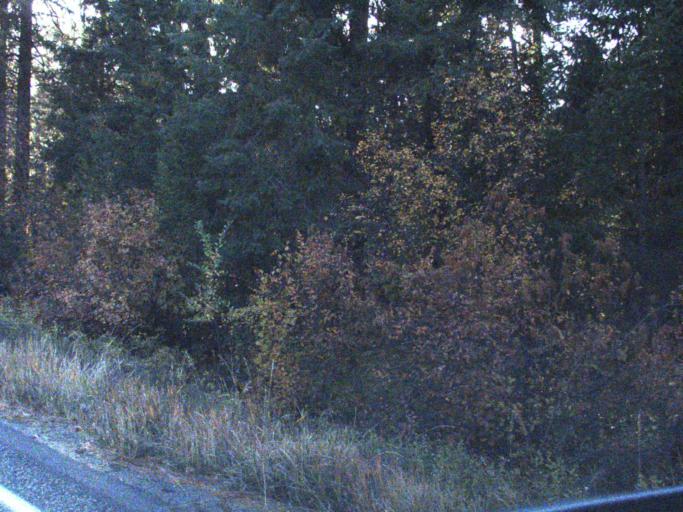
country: US
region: Washington
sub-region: Stevens County
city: Kettle Falls
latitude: 48.8207
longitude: -117.9186
